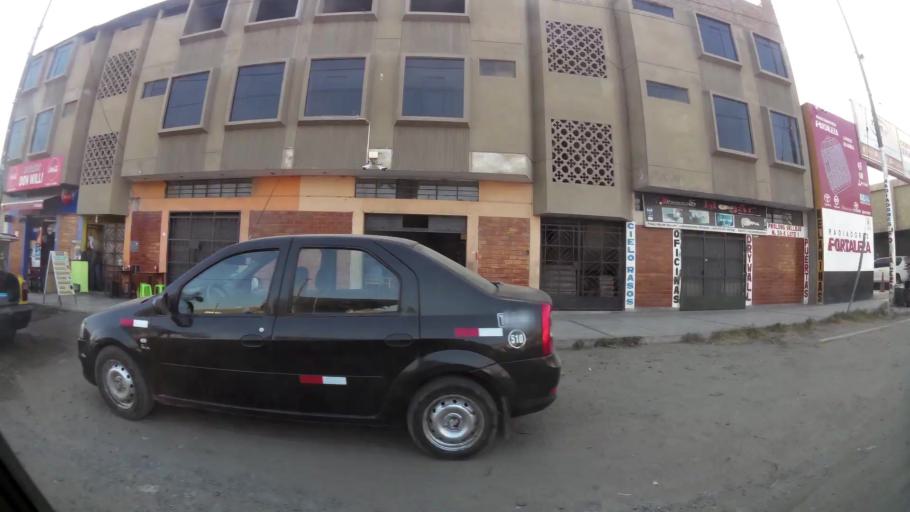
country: PE
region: La Libertad
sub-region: Provincia de Trujillo
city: El Porvenir
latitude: -8.0937
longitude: -79.0042
